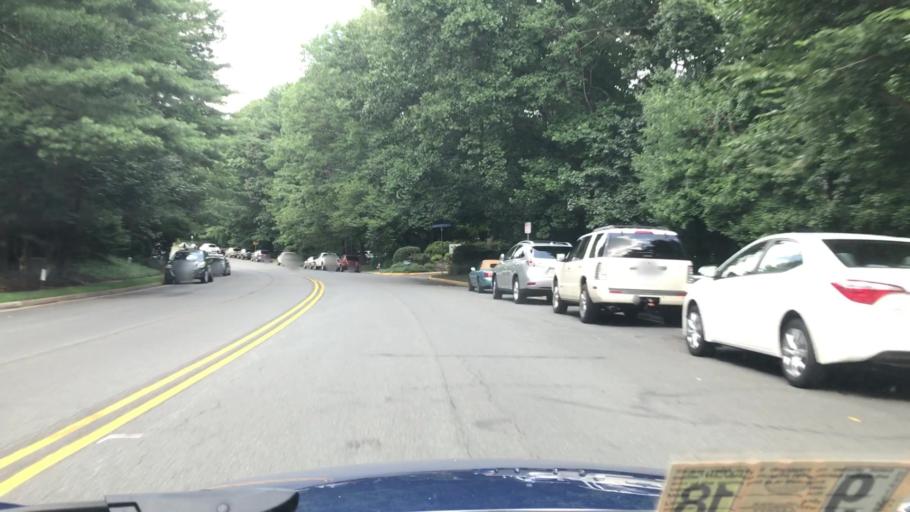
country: US
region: Virginia
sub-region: Fairfax County
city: Reston
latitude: 38.9355
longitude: -77.3350
